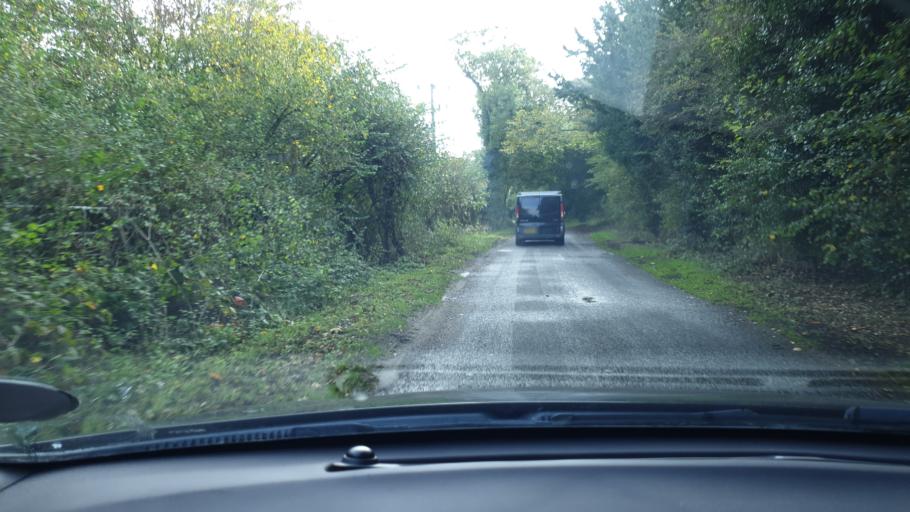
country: GB
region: England
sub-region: Essex
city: Alresford
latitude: 51.8588
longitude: 1.0252
